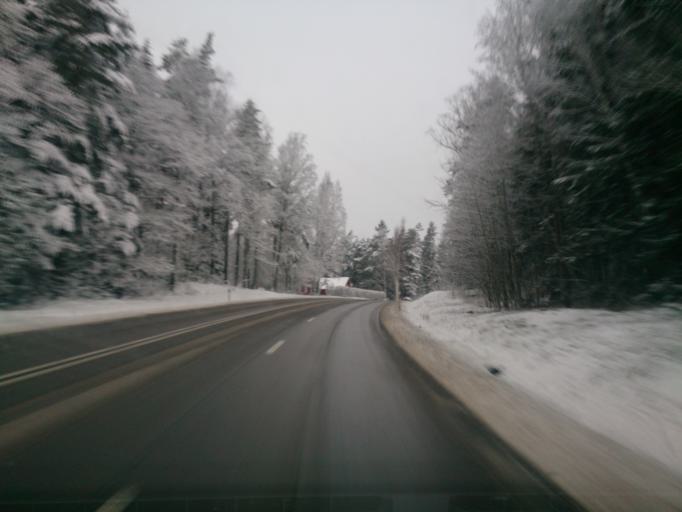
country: SE
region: OEstergoetland
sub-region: Atvidabergs Kommun
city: Atvidaberg
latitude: 58.2625
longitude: 15.9243
